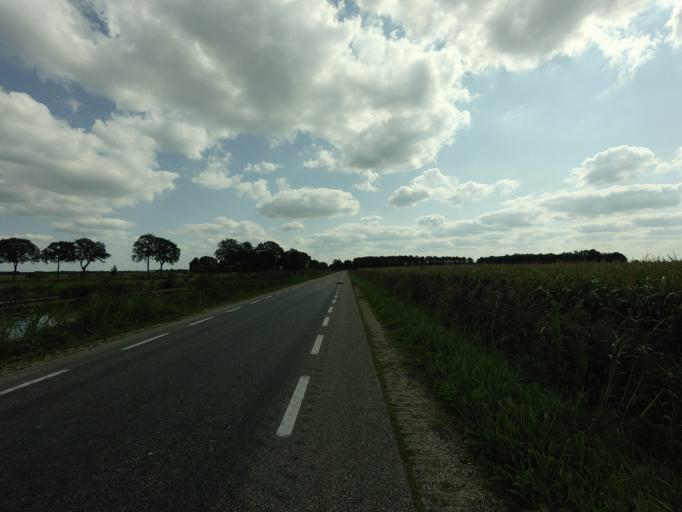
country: NL
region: Drenthe
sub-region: Gemeente Westerveld
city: Dwingeloo
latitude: 52.8770
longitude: 6.4325
